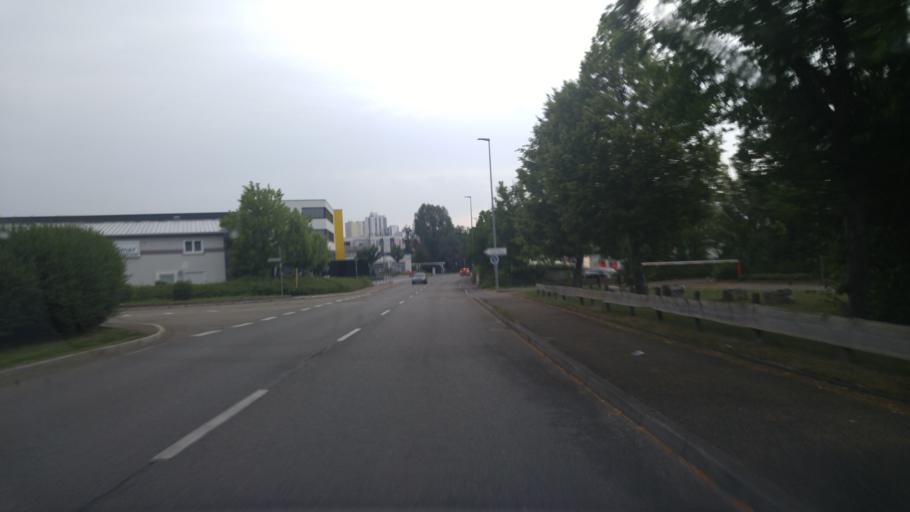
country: DE
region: Baden-Wuerttemberg
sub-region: Regierungsbezirk Stuttgart
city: Leonberg
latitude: 48.7848
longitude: 9.0068
